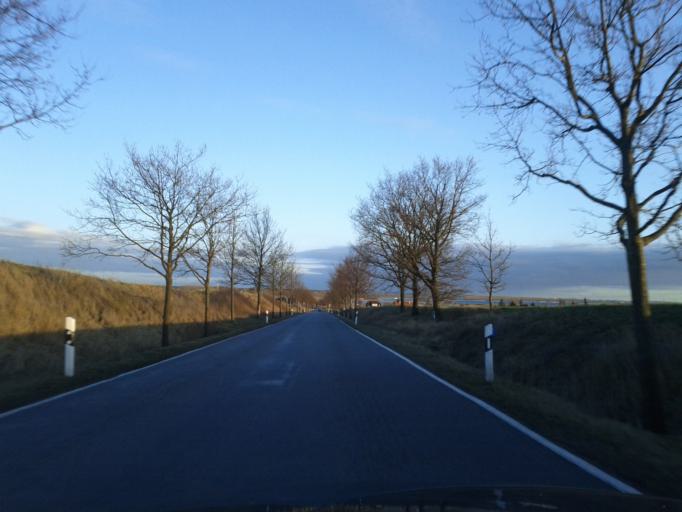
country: DE
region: Mecklenburg-Vorpommern
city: Blowatz
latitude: 53.9780
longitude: 11.4595
